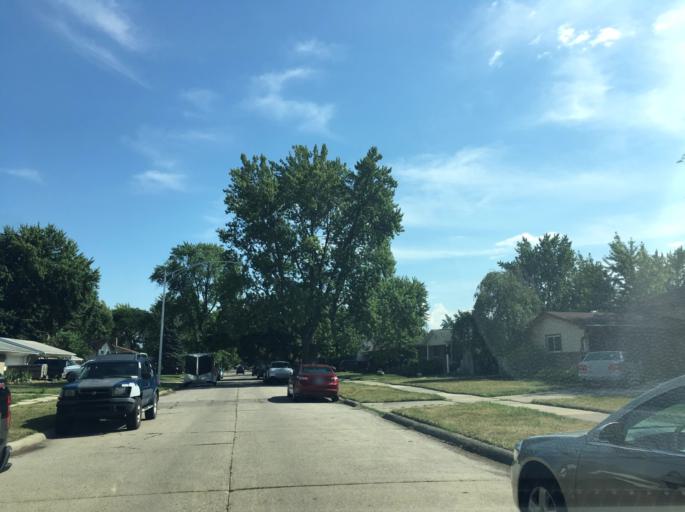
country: US
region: Michigan
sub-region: Macomb County
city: Fraser
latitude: 42.5520
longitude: -82.9212
